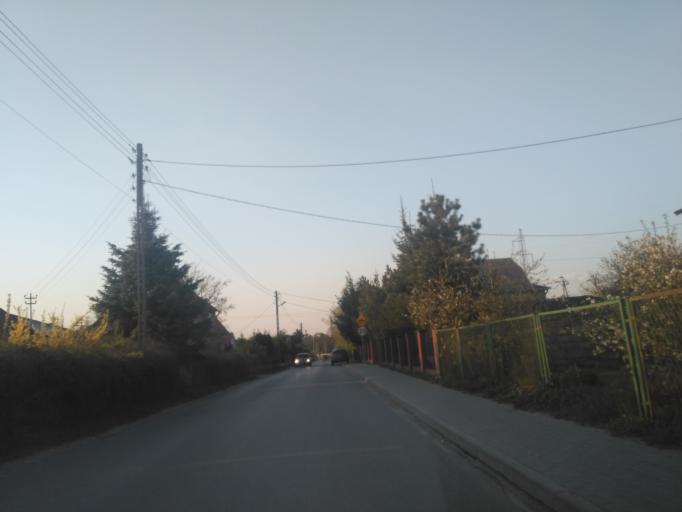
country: PL
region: Lublin Voivodeship
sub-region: Powiat chelmski
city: Pokrowka
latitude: 51.1149
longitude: 23.4839
